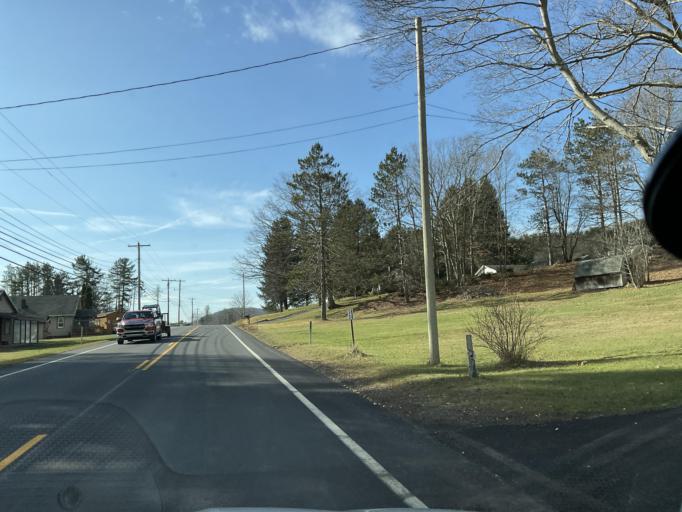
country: US
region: Maryland
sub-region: Garrett County
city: Oakland
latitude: 39.4045
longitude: -79.4215
